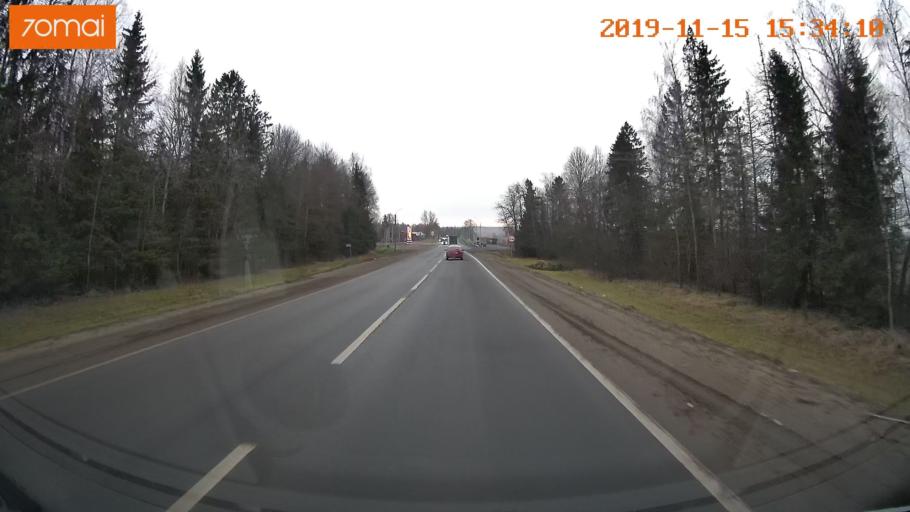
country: RU
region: Jaroslavl
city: Danilov
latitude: 58.0722
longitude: 40.0898
